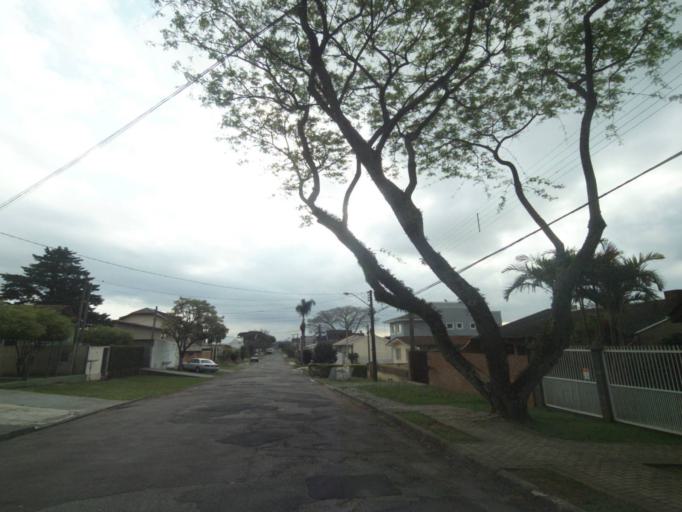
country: BR
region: Parana
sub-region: Pinhais
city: Pinhais
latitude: -25.4138
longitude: -49.2123
